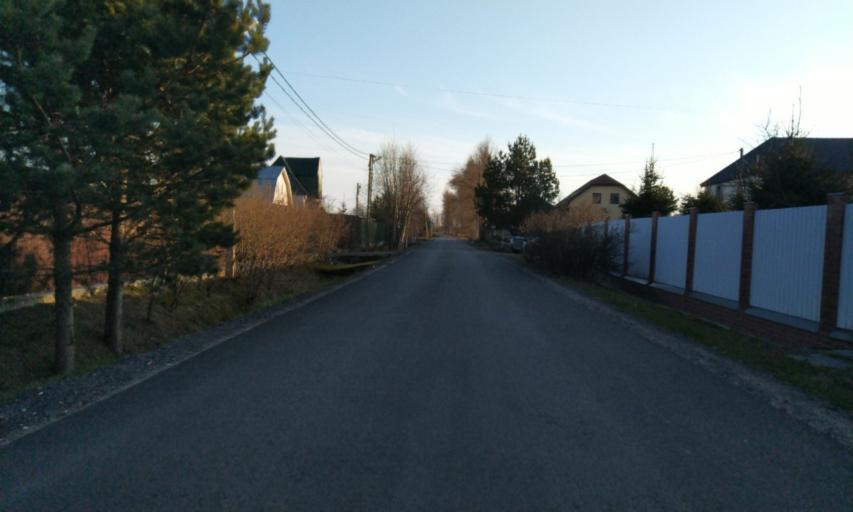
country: RU
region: Leningrad
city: Novoye Devyatkino
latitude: 60.1056
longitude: 30.4520
